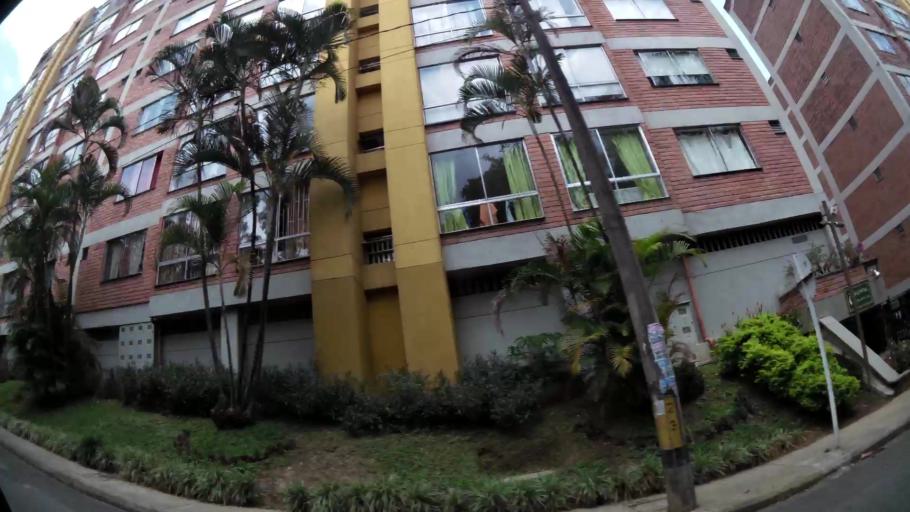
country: CO
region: Antioquia
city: Medellin
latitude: 6.2454
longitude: -75.6133
